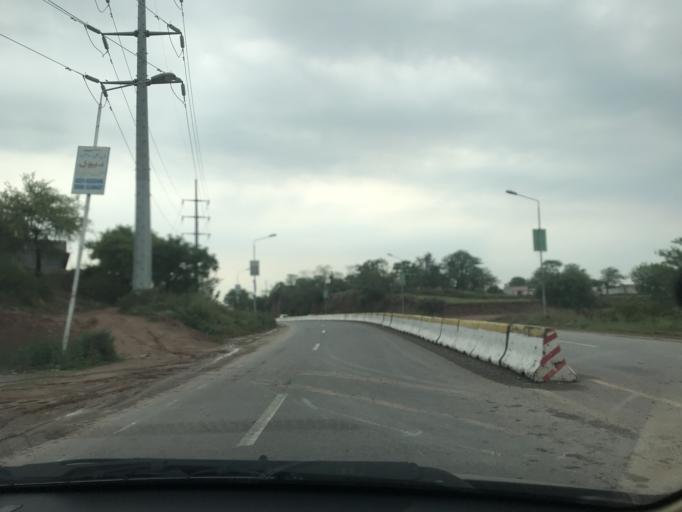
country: PK
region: Islamabad
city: Islamabad
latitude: 33.6936
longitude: 73.1742
